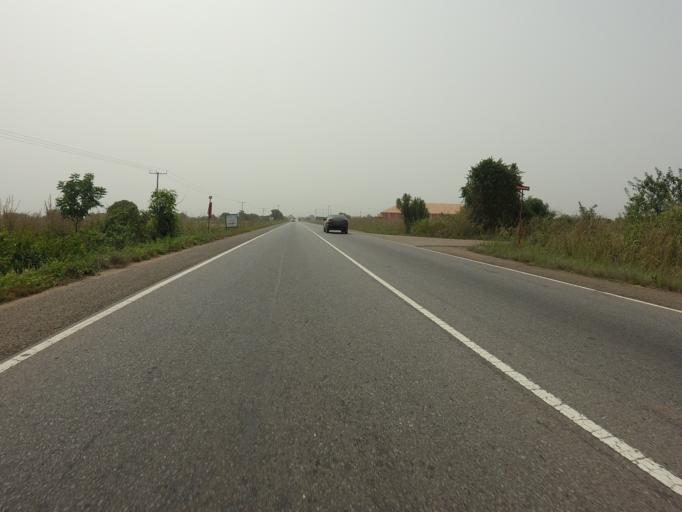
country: GH
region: Volta
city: Anloga
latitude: 5.9315
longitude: 0.5233
